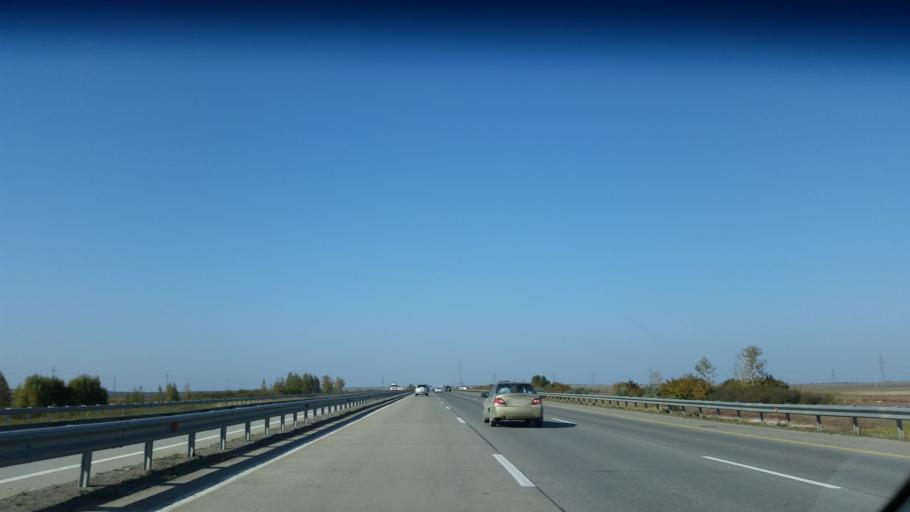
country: KZ
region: Astana Qalasy
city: Astana
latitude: 51.2787
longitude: 71.3642
